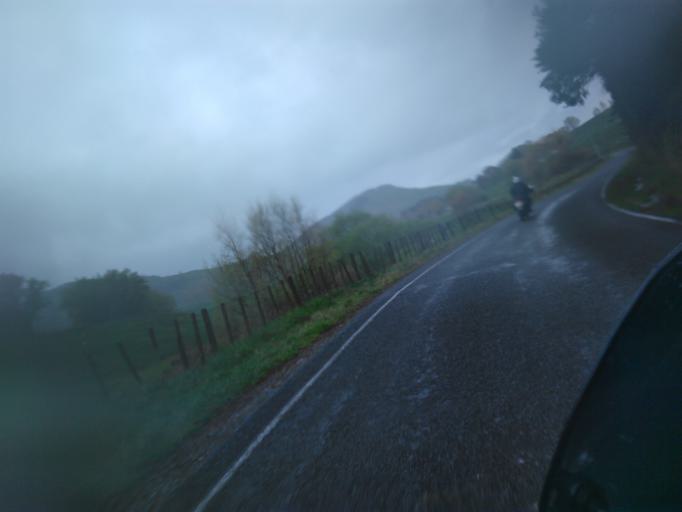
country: NZ
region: Gisborne
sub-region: Gisborne District
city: Gisborne
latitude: -38.6744
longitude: 177.7215
